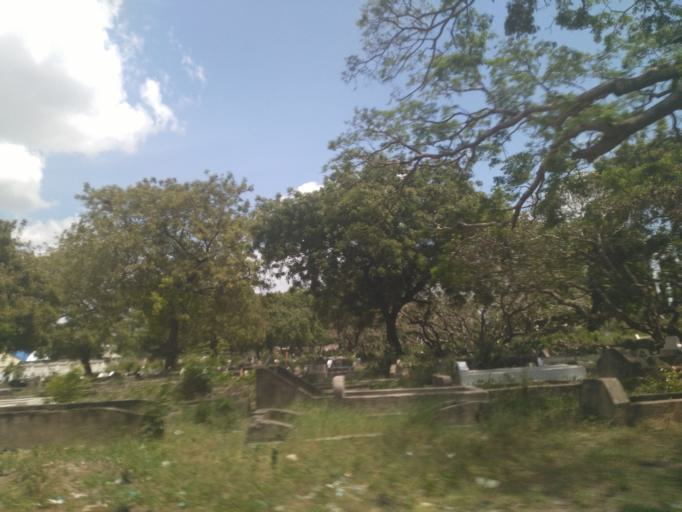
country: TZ
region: Dar es Salaam
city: Dar es Salaam
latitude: -6.8444
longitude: 39.2649
